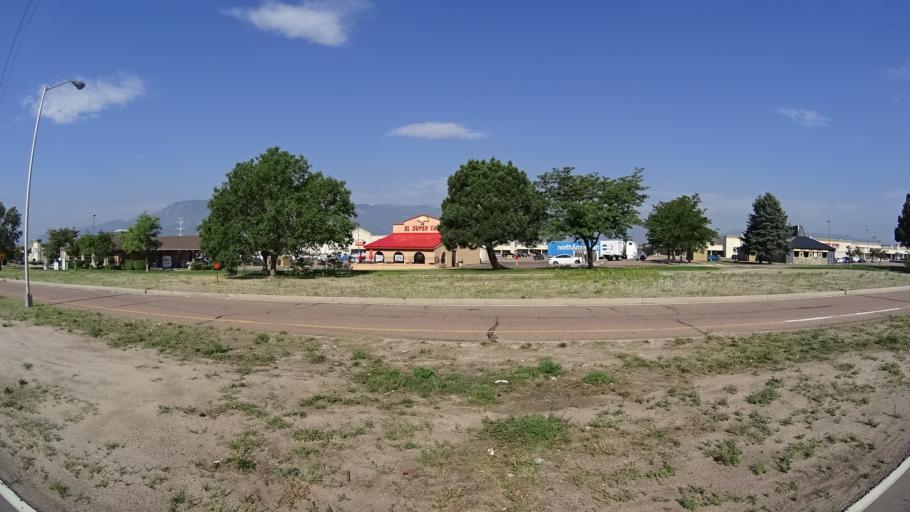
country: US
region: Colorado
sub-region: El Paso County
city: Stratmoor
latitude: 38.7908
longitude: -104.7576
